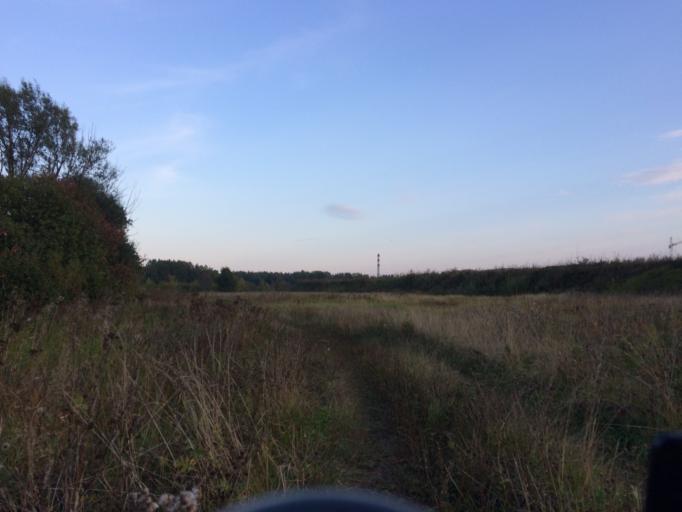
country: RU
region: Mariy-El
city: Yoshkar-Ola
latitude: 56.6497
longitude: 47.9229
